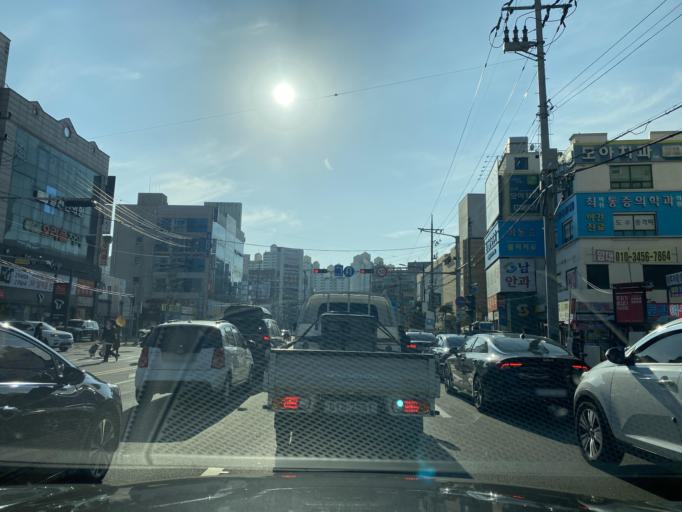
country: KR
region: Chungcheongnam-do
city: Cheonan
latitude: 36.7964
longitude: 127.1289
